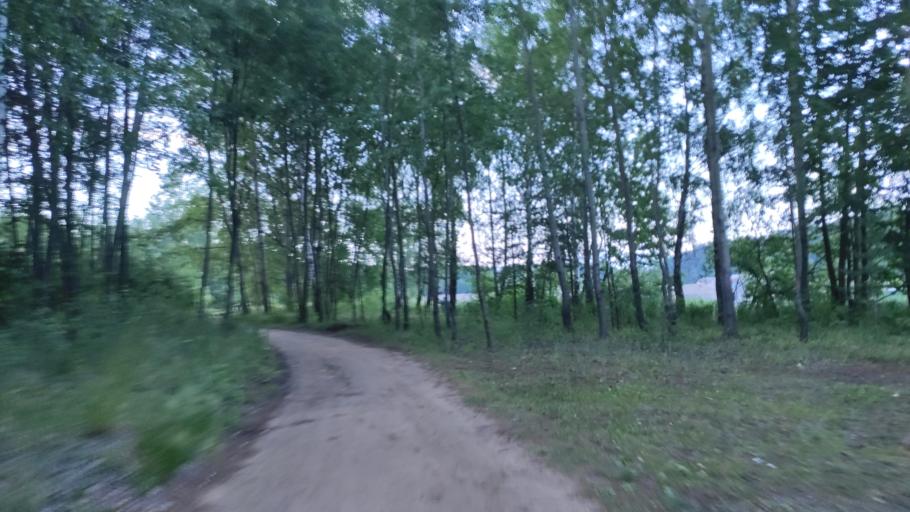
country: BY
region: Minsk
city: Zhdanovichy
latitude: 53.9505
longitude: 27.4808
